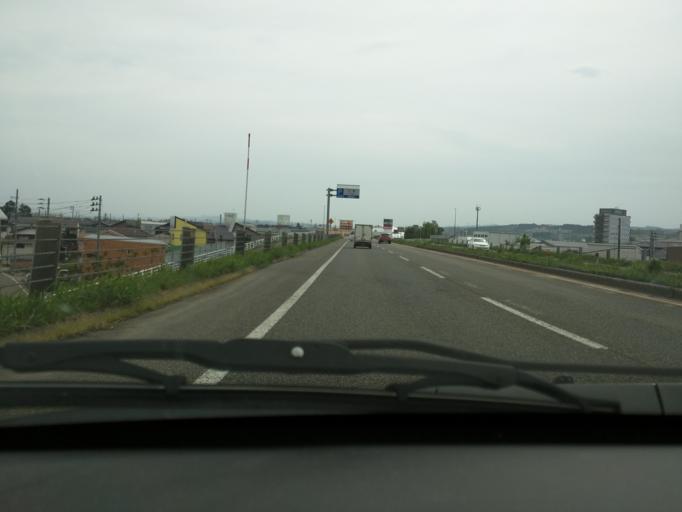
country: JP
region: Niigata
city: Nagaoka
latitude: 37.4508
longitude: 138.8011
